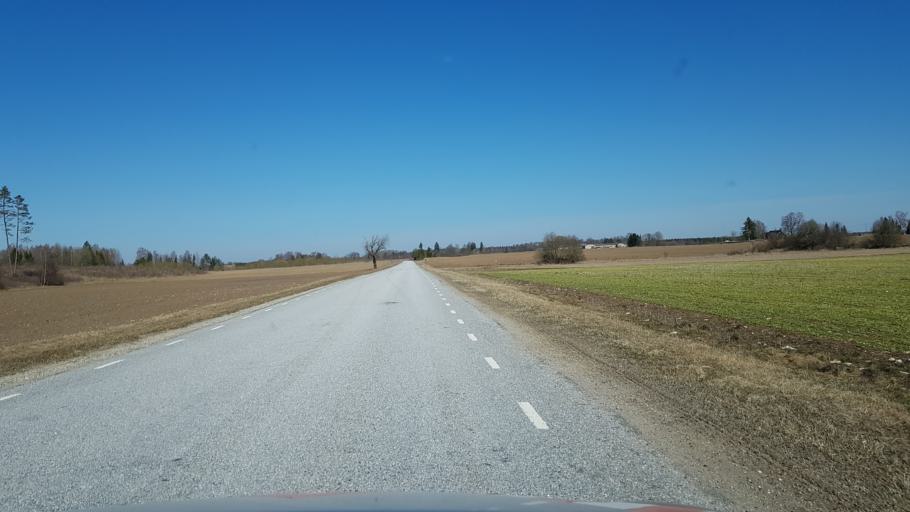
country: EE
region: Jaervamaa
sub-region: Koeru vald
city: Koeru
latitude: 59.0257
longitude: 26.0888
